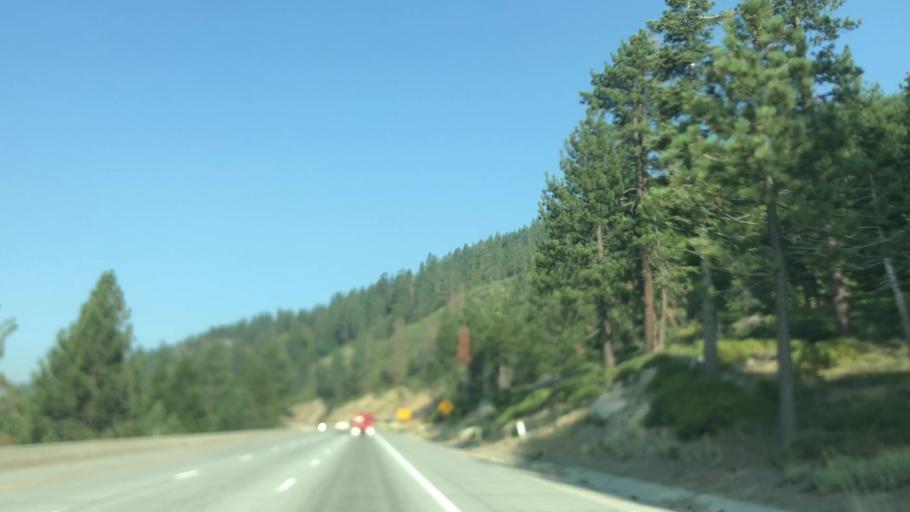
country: US
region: California
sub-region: Nevada County
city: Truckee
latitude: 39.3318
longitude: -120.2538
